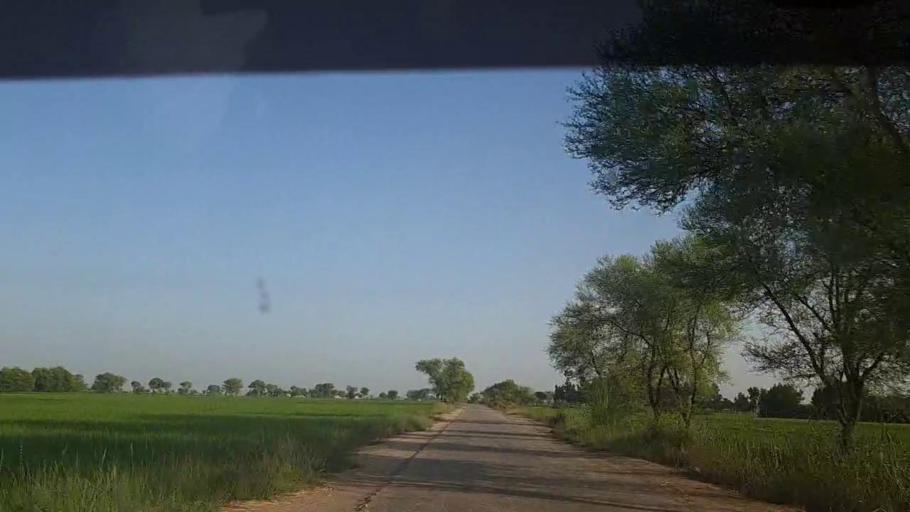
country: PK
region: Sindh
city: Thul
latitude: 28.2073
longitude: 68.8712
